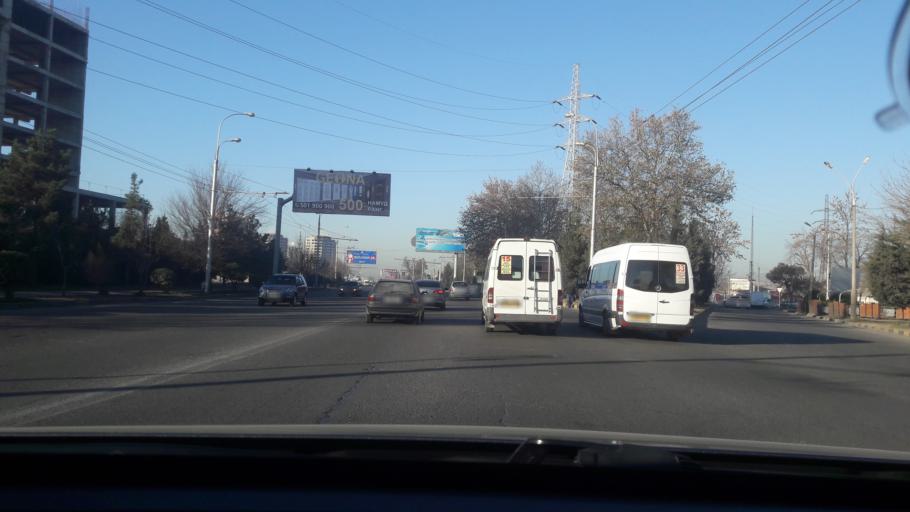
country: TJ
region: Dushanbe
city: Dushanbe
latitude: 38.5615
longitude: 68.7768
